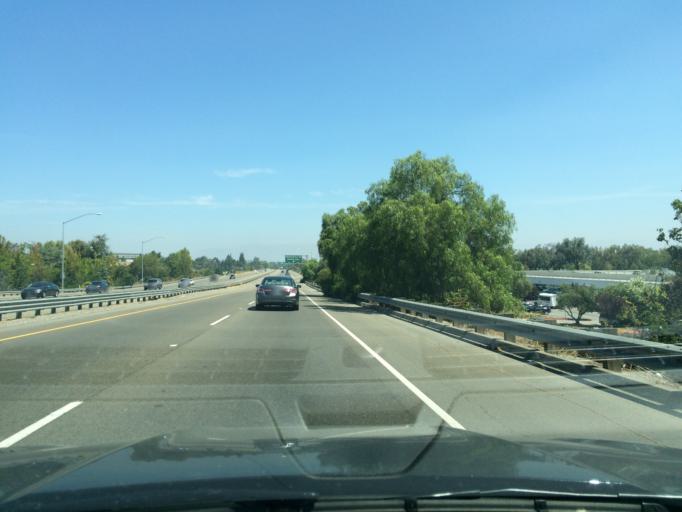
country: US
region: California
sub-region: Santa Clara County
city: Sunnyvale
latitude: 37.3887
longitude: -122.0557
